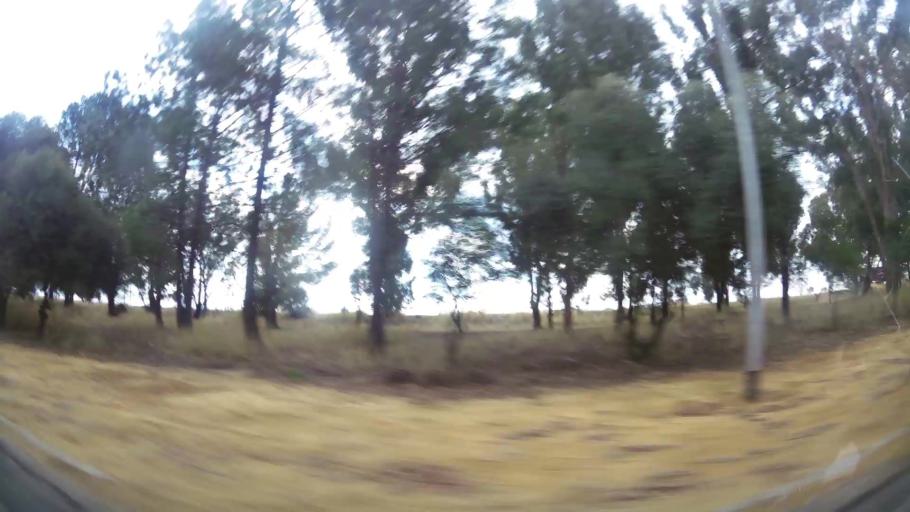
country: ZA
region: Orange Free State
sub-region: Fezile Dabi District Municipality
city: Sasolburg
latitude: -26.7906
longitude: 27.8176
